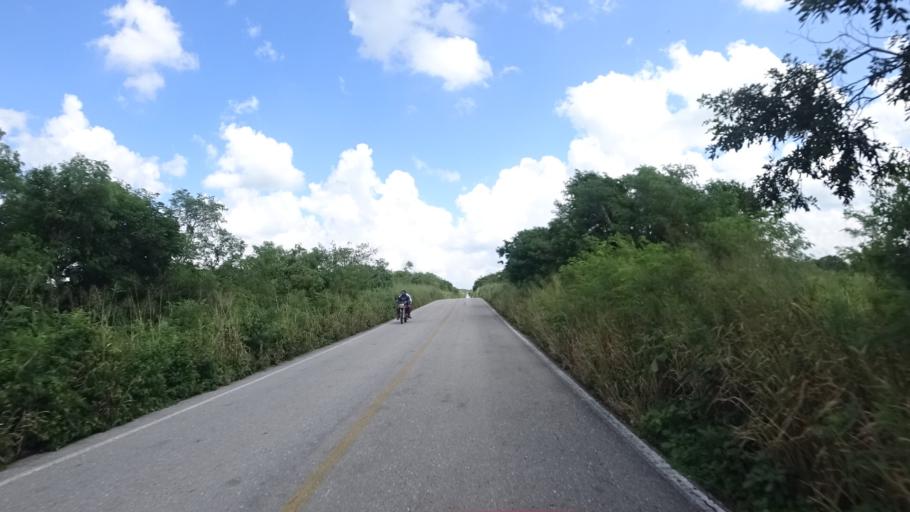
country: MX
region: Yucatan
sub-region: Panaba
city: Loche
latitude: 21.4223
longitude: -88.1418
